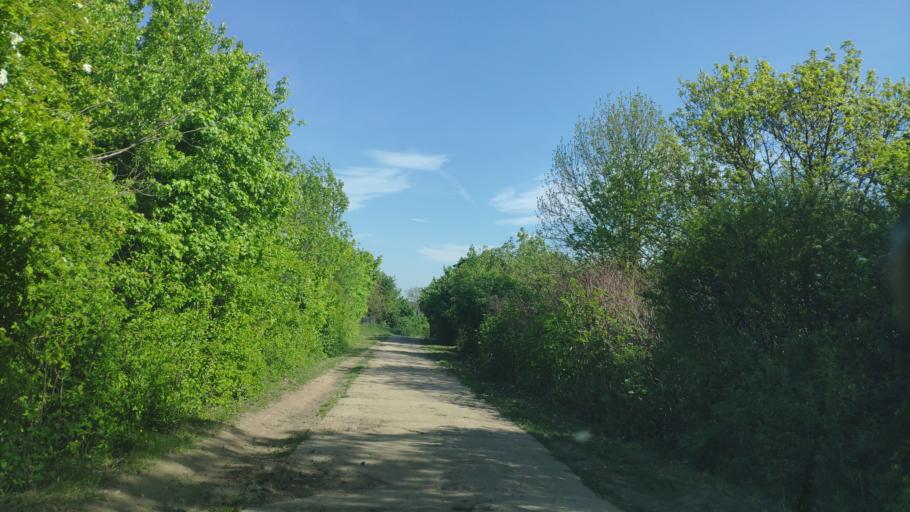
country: SK
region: Kosicky
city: Secovce
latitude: 48.6859
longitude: 21.6075
